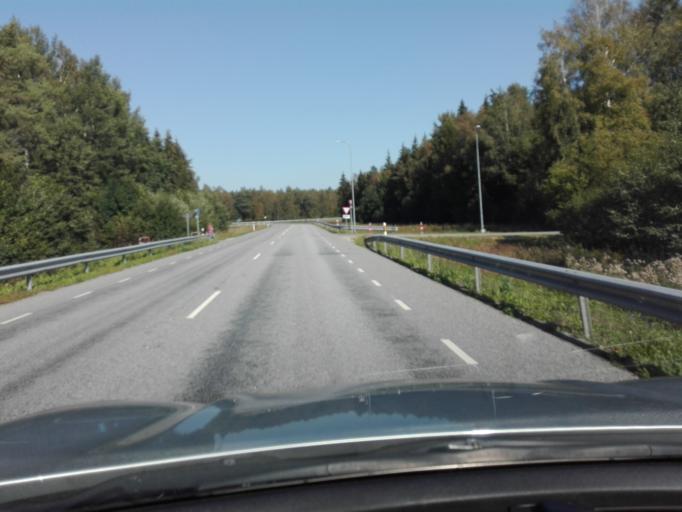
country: EE
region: Raplamaa
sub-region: Rapla vald
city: Rapla
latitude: 59.0172
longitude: 24.7799
